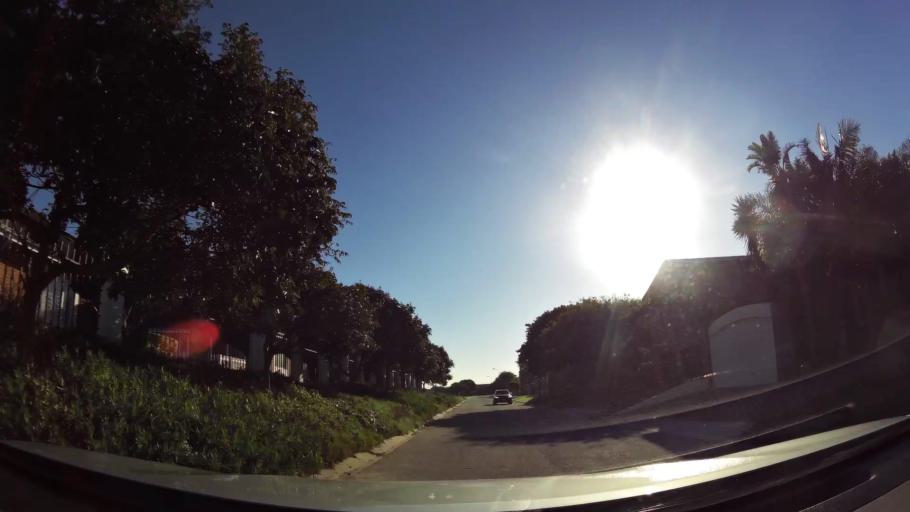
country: ZA
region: Eastern Cape
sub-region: Nelson Mandela Bay Metropolitan Municipality
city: Port Elizabeth
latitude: -33.9939
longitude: 25.6465
